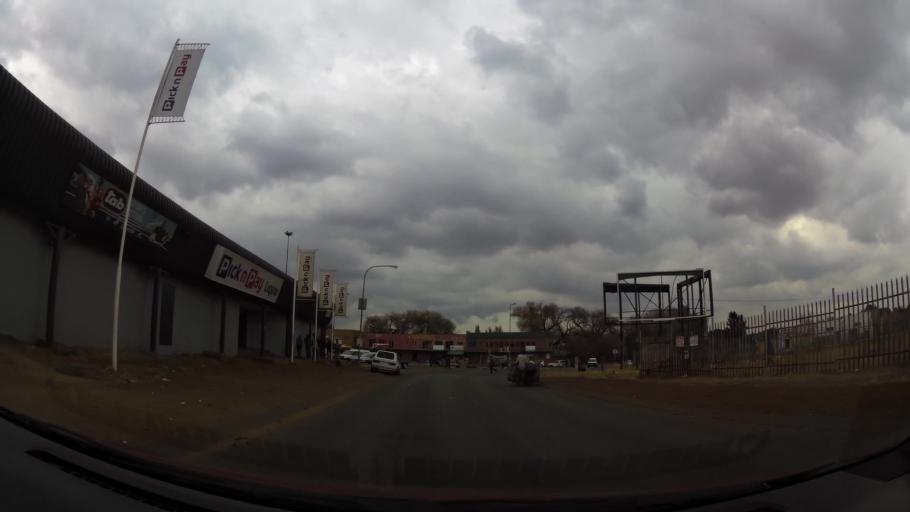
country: ZA
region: Gauteng
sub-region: City of Johannesburg Metropolitan Municipality
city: Soweto
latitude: -26.2609
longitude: 27.8467
